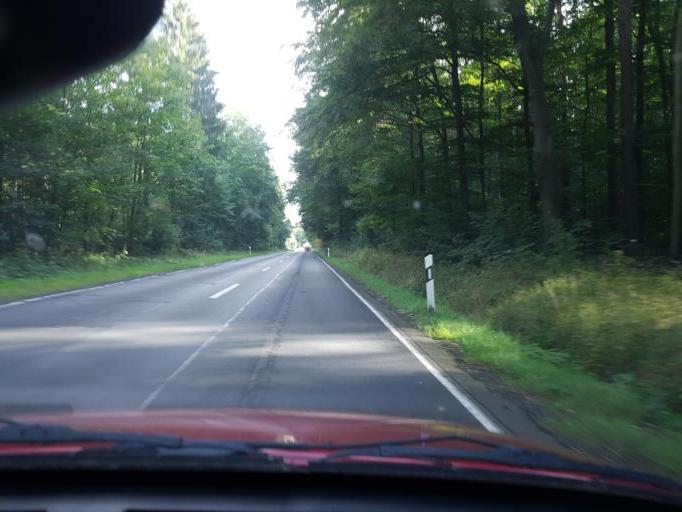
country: DE
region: Hesse
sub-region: Regierungsbezirk Giessen
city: Alten Buseck
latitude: 50.5876
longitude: 8.7313
